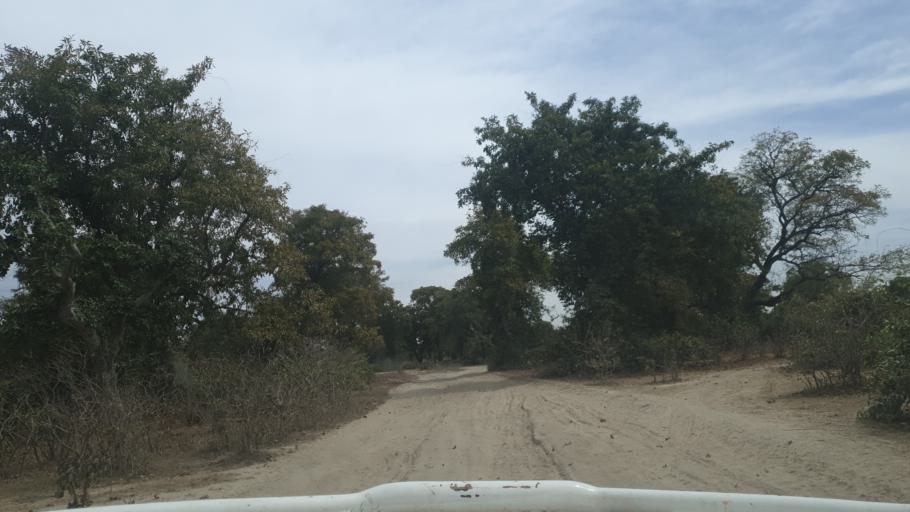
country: ML
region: Sikasso
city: Yorosso
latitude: 12.2378
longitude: -4.7385
